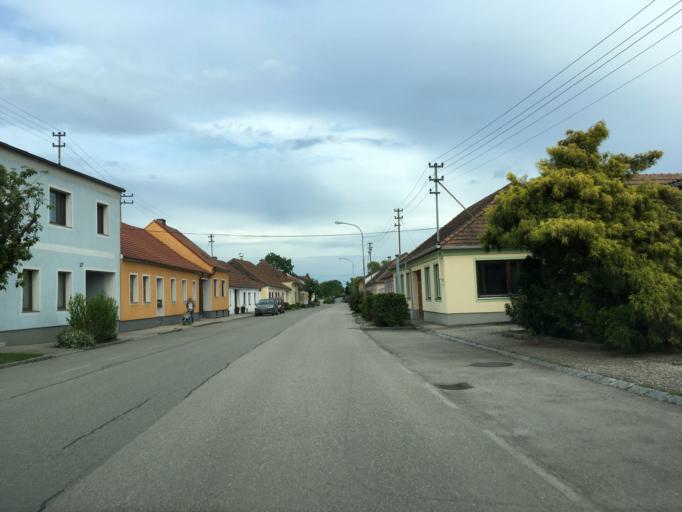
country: AT
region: Lower Austria
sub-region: Politischer Bezirk Tulln
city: Kirchberg am Wagram
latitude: 48.4075
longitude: 15.8931
